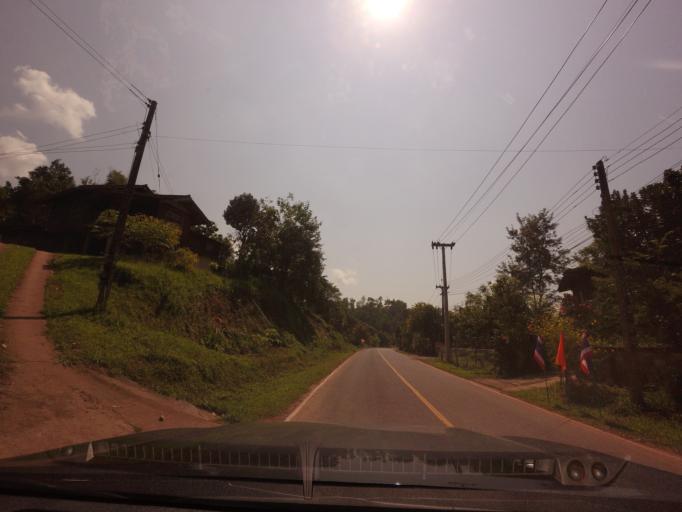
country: TH
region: Nan
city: Bo Kluea
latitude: 19.0765
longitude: 101.1590
